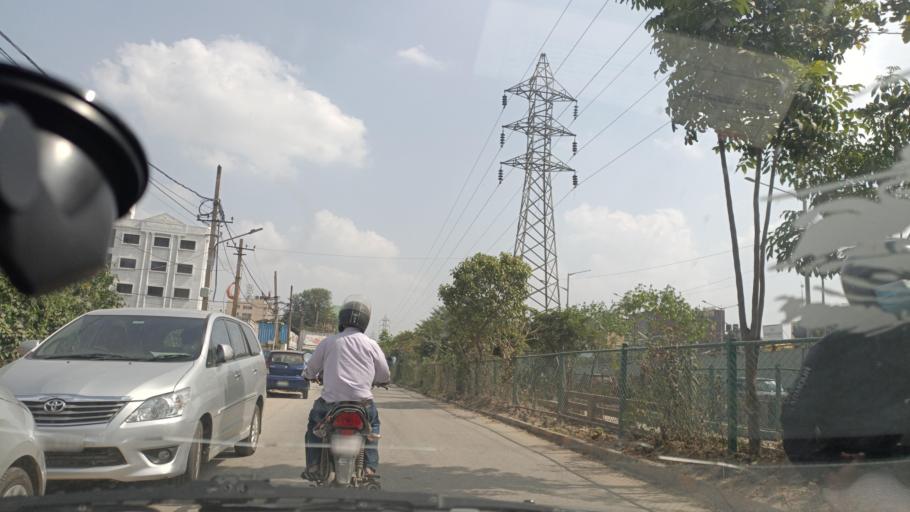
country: IN
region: Karnataka
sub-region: Bangalore Urban
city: Bangalore
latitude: 13.0239
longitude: 77.6452
